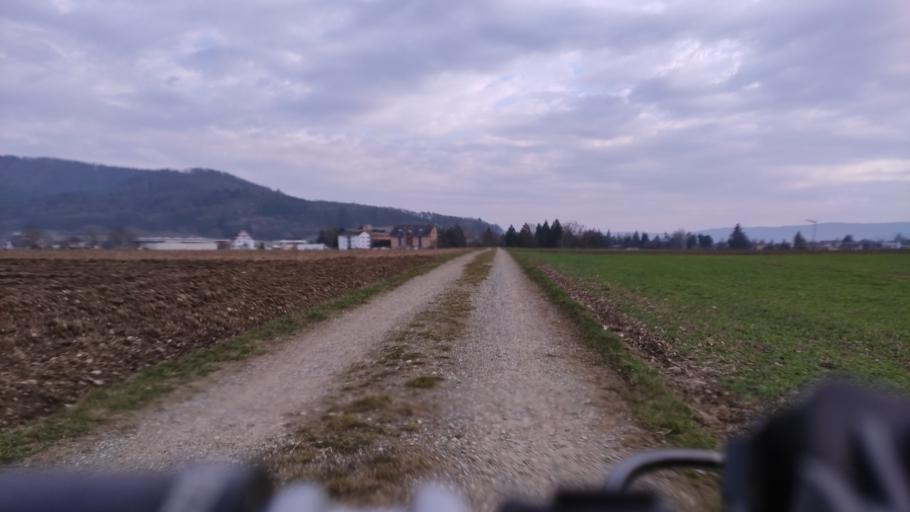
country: CH
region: Schaffhausen
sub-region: Bezirk Stein
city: Ramsen
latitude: 47.7149
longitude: 8.8181
